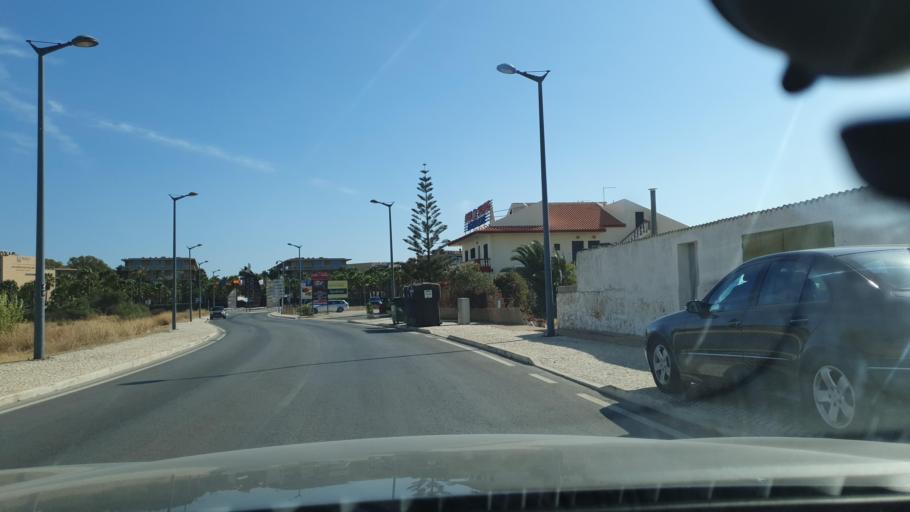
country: PT
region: Faro
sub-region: Albufeira
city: Guia
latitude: 37.0965
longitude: -8.3185
